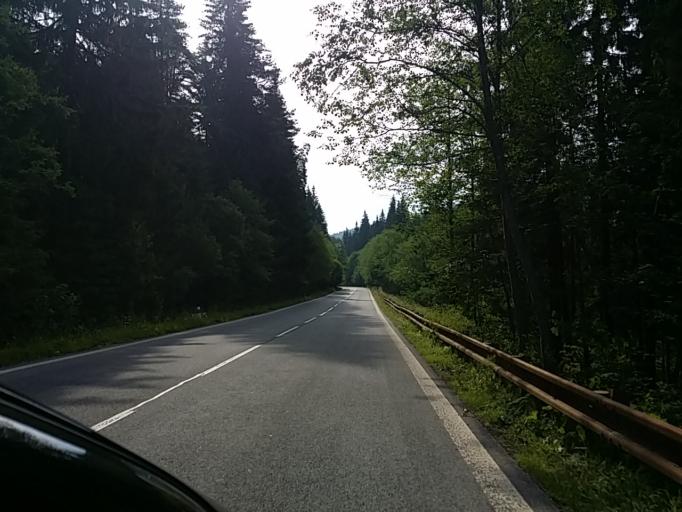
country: SK
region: Kosicky
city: Dobsina
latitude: 48.8740
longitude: 20.2688
